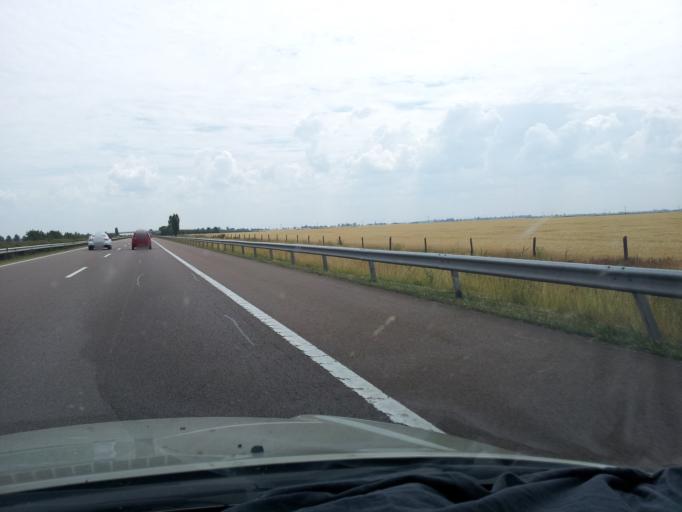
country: HU
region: Borsod-Abauj-Zemplen
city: Mezokovesd
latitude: 47.7722
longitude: 20.5519
